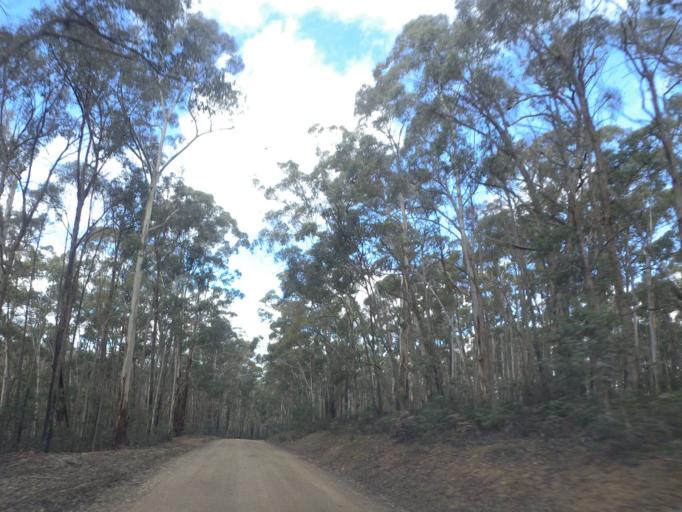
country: AU
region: Victoria
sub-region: Moorabool
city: Bacchus Marsh
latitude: -37.4653
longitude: 144.4809
